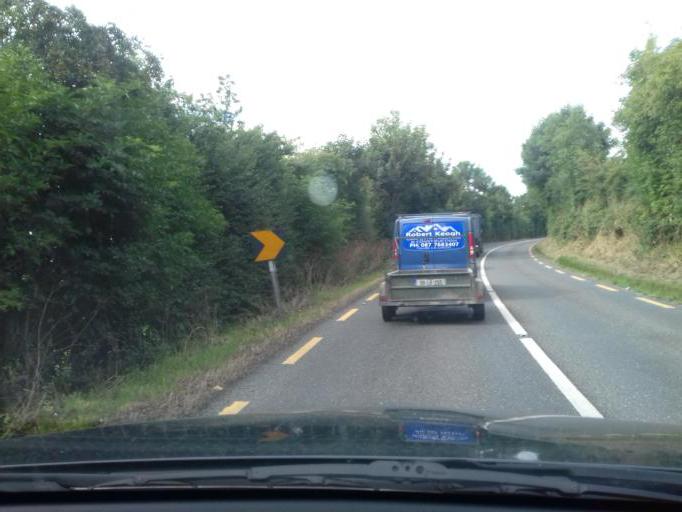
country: IE
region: Leinster
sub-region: Wicklow
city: Baltinglass
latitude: 52.9127
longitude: -6.7011
